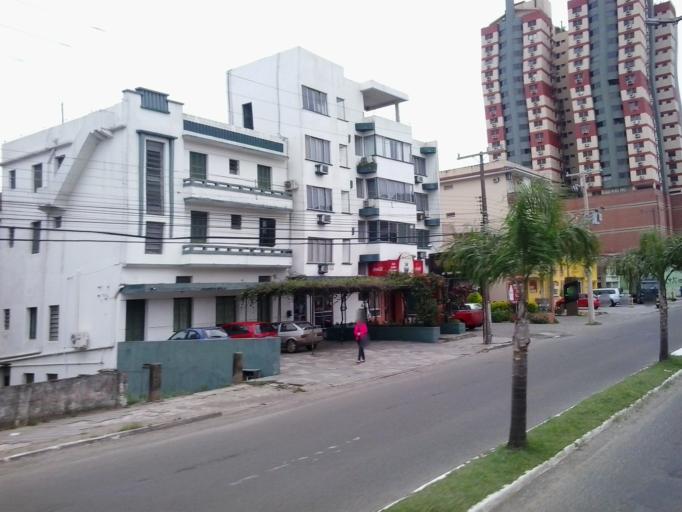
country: BR
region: Rio Grande do Sul
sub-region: Santa Maria
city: Santa Maria
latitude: -29.6894
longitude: -53.7935
